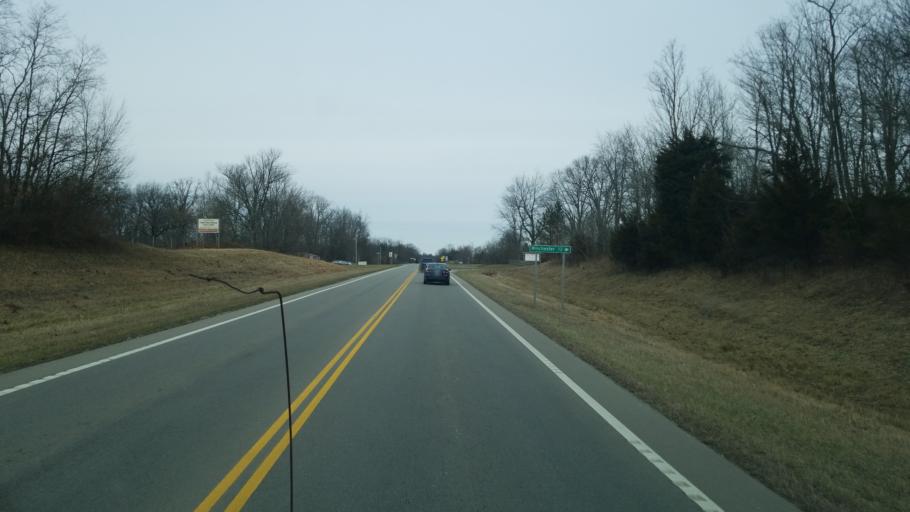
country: US
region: Ohio
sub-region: Highland County
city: Hillsboro
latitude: 39.1146
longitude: -83.6756
